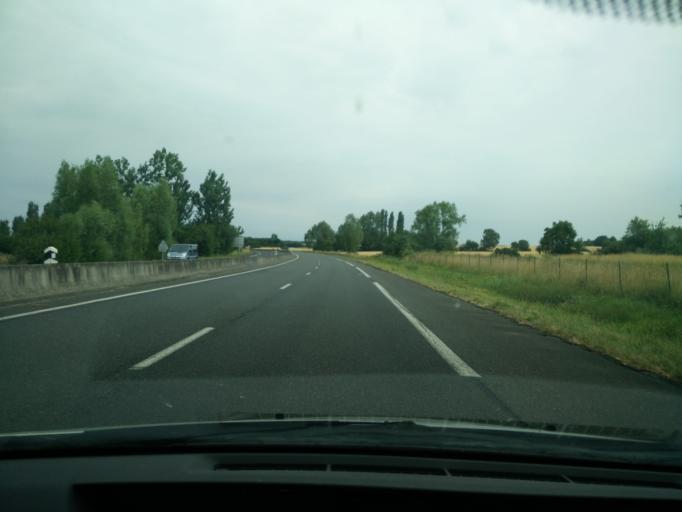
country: FR
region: Pays de la Loire
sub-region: Departement de Maine-et-Loire
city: Saint-Jean
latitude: 47.2411
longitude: -0.3210
